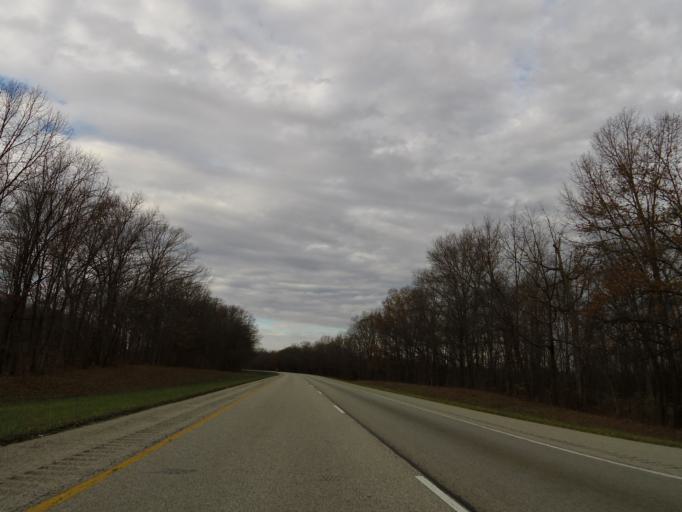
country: US
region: Illinois
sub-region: Washington County
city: Nashville
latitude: 38.3918
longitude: -89.3104
